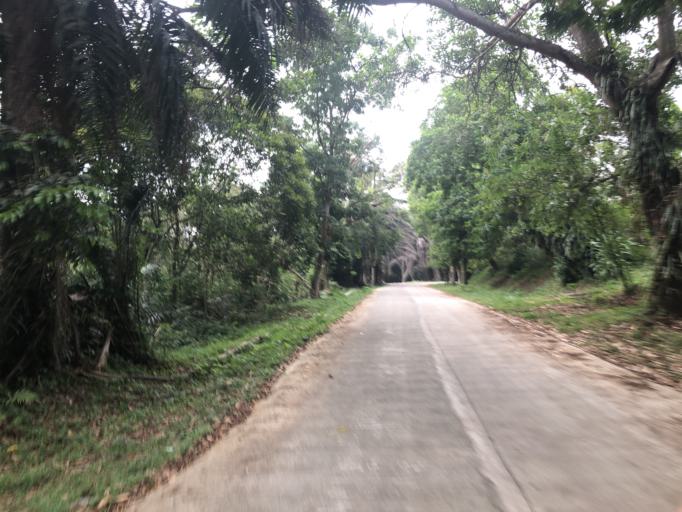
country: ID
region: West Java
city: Ciampea
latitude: -6.5511
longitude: 106.7136
